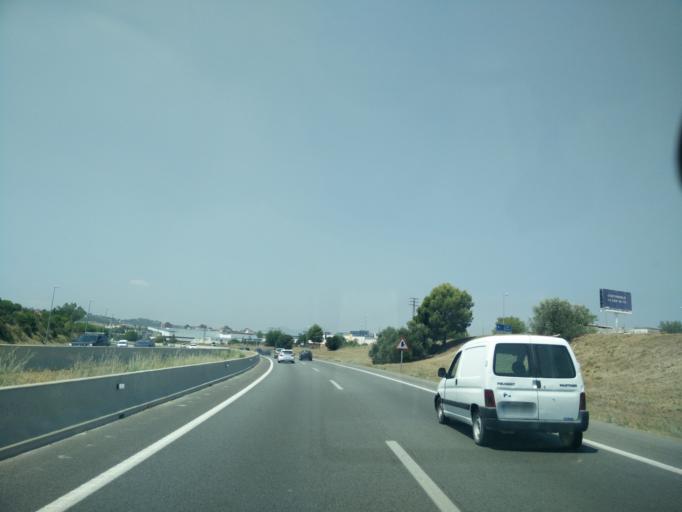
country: ES
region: Catalonia
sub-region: Provincia de Barcelona
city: Terrassa
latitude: 41.5458
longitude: 2.0367
